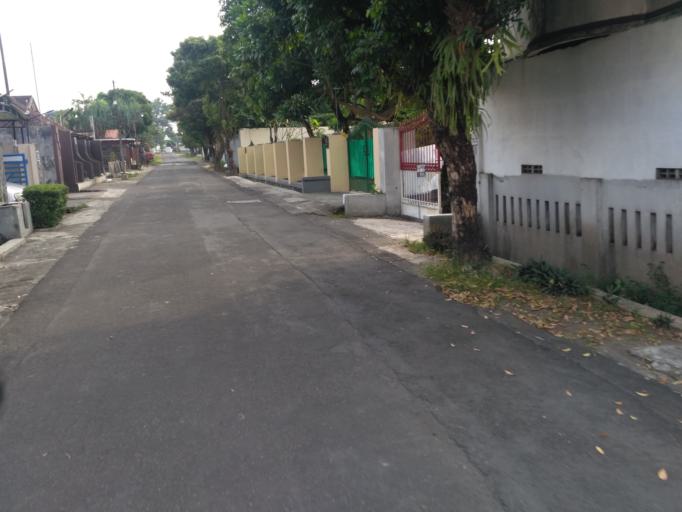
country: ID
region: Daerah Istimewa Yogyakarta
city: Melati
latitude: -7.7360
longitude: 110.3883
